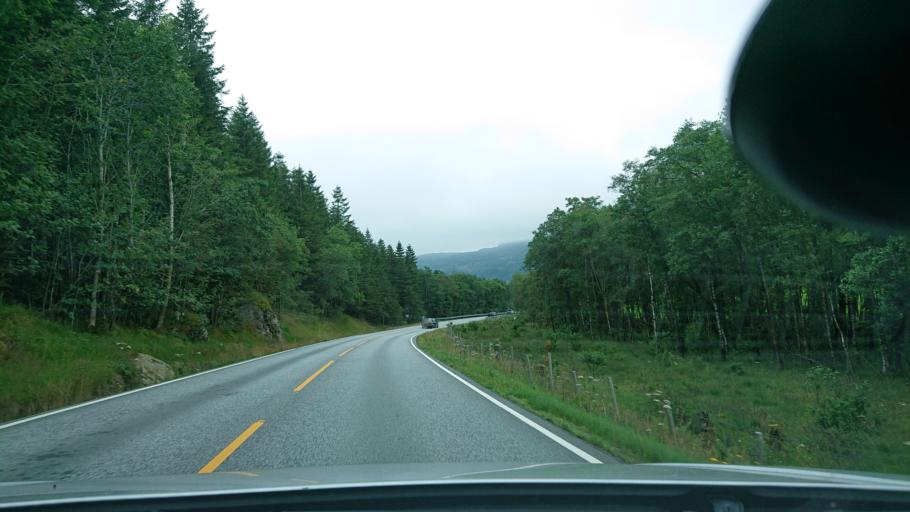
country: NO
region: Rogaland
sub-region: Hjelmeland
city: Hjelmelandsvagen
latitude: 59.1652
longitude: 6.1418
